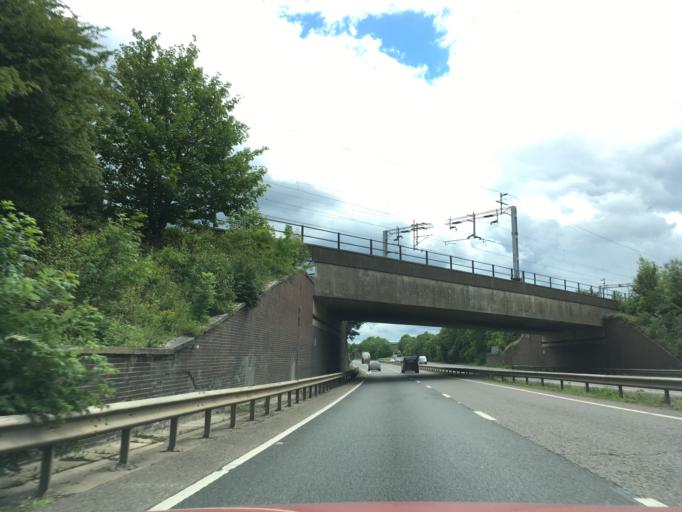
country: GB
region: England
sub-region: Buckinghamshire
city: Bletchley
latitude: 52.0125
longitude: -0.7472
